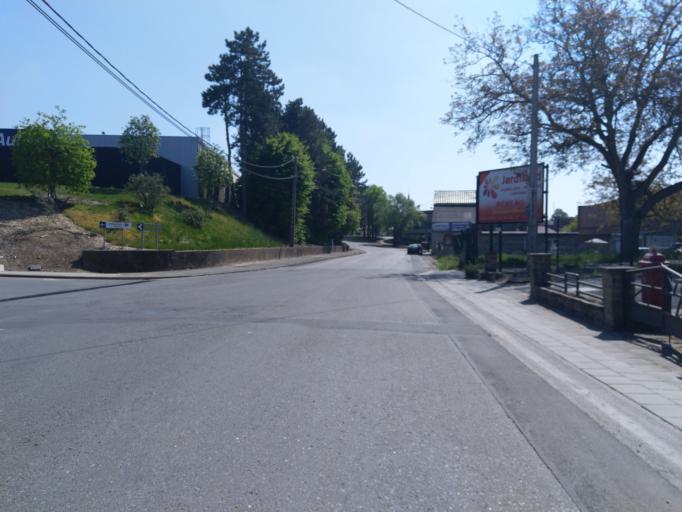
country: BE
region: Wallonia
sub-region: Province du Hainaut
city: Soignies
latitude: 50.5850
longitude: 4.0703
